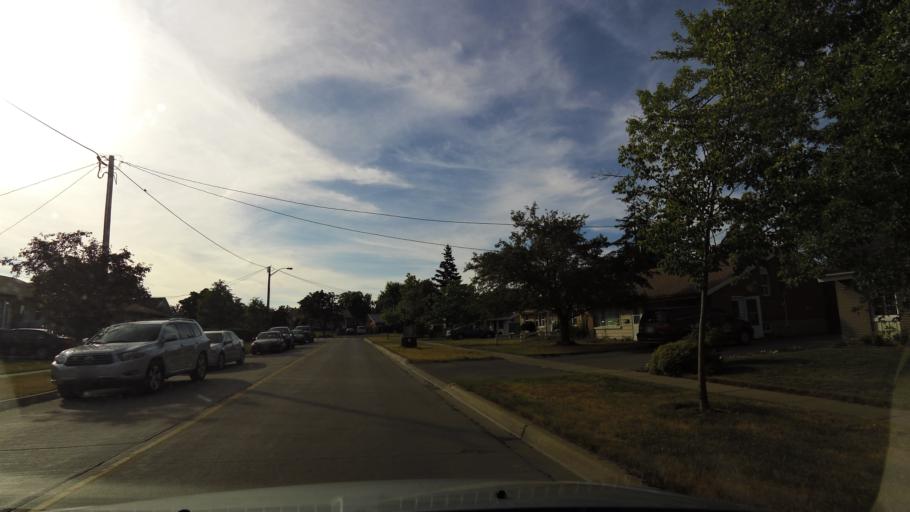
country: CA
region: Ontario
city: Brampton
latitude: 43.6879
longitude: -79.7422
